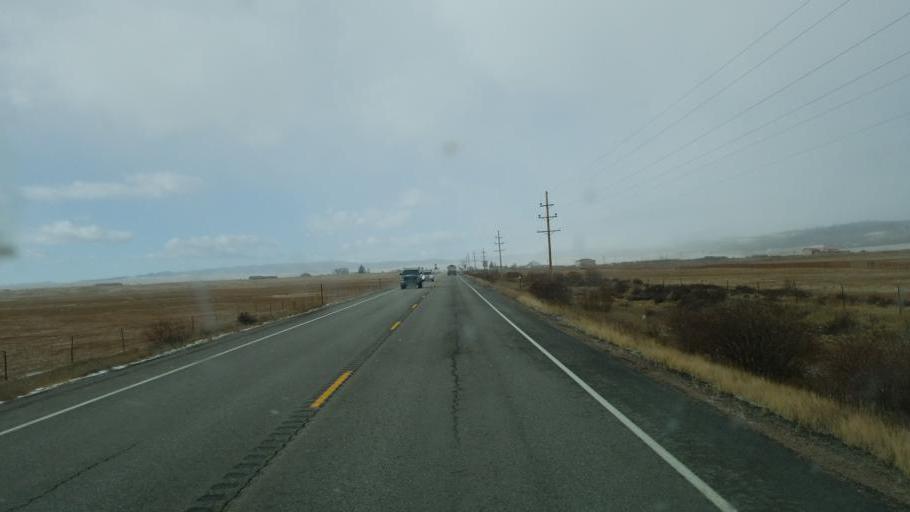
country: US
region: Colorado
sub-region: Park County
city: Fairplay
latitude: 39.3831
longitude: -105.7940
